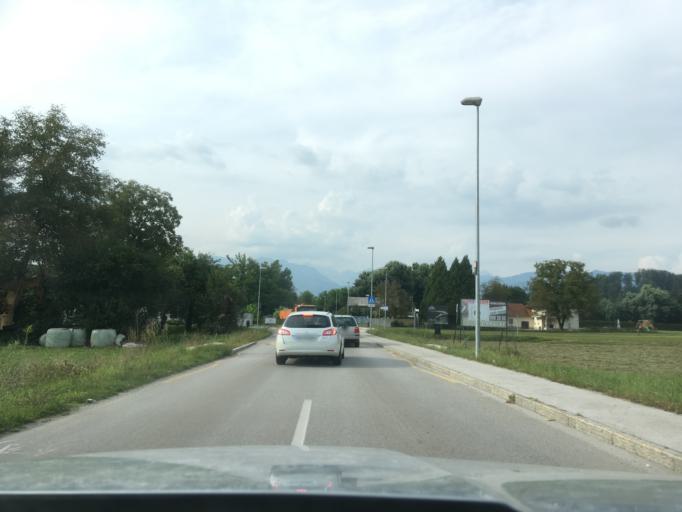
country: SI
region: Domzale
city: Radomlje
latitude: 46.1809
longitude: 14.6089
